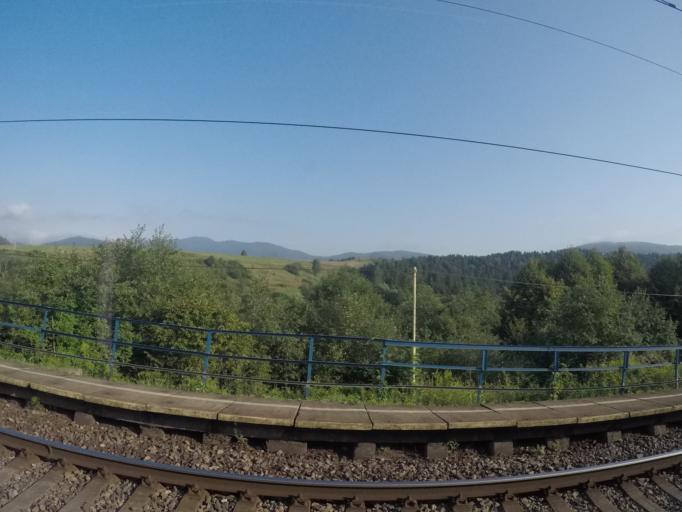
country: SK
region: Kosicky
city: Gelnica
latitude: 48.9138
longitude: 20.9469
